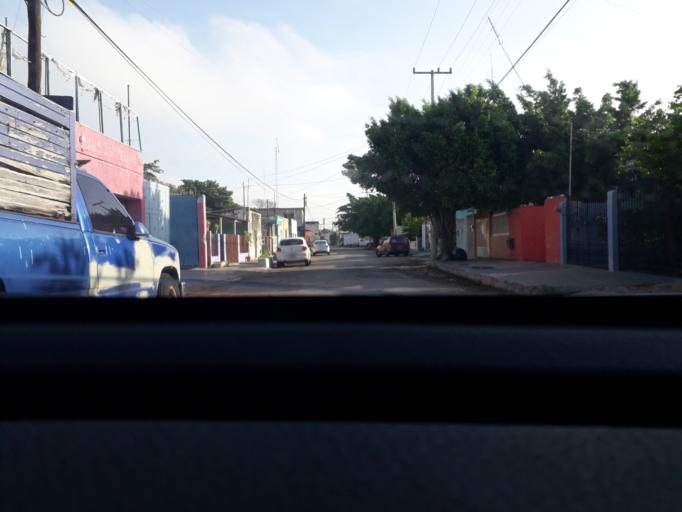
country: MX
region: Yucatan
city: Merida
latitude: 20.9614
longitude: -89.6353
